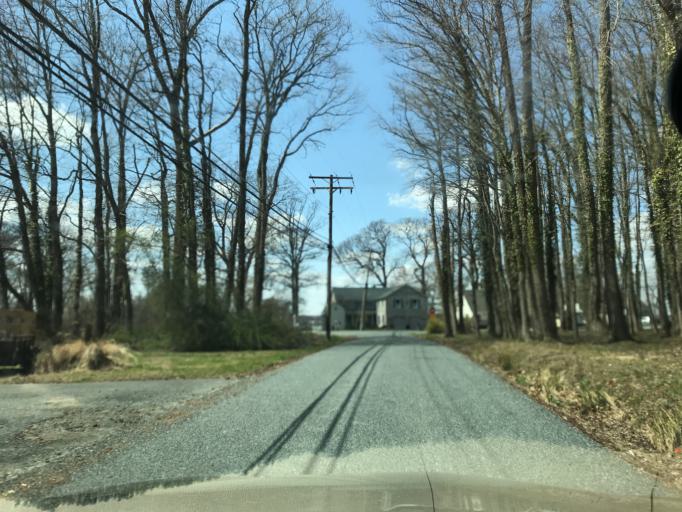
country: US
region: Maryland
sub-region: Harford County
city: Riverside
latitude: 39.4501
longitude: -76.2306
